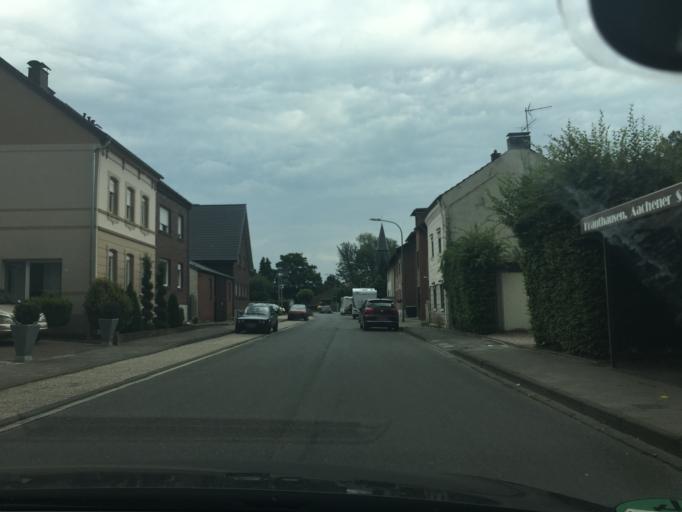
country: DE
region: North Rhine-Westphalia
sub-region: Regierungsbezirk Koln
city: Niederzier
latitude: 50.8761
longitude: 6.4226
